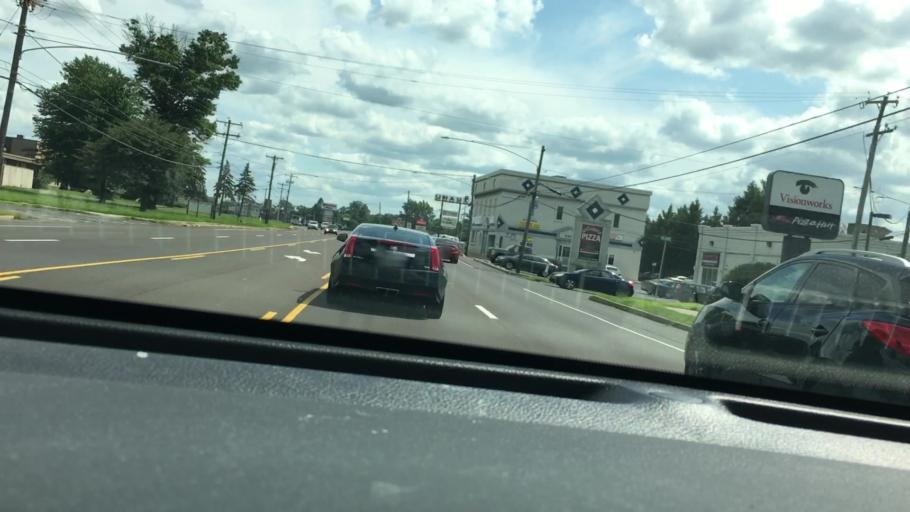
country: US
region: Pennsylvania
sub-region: Bucks County
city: Eddington
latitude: 40.1021
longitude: -74.9495
